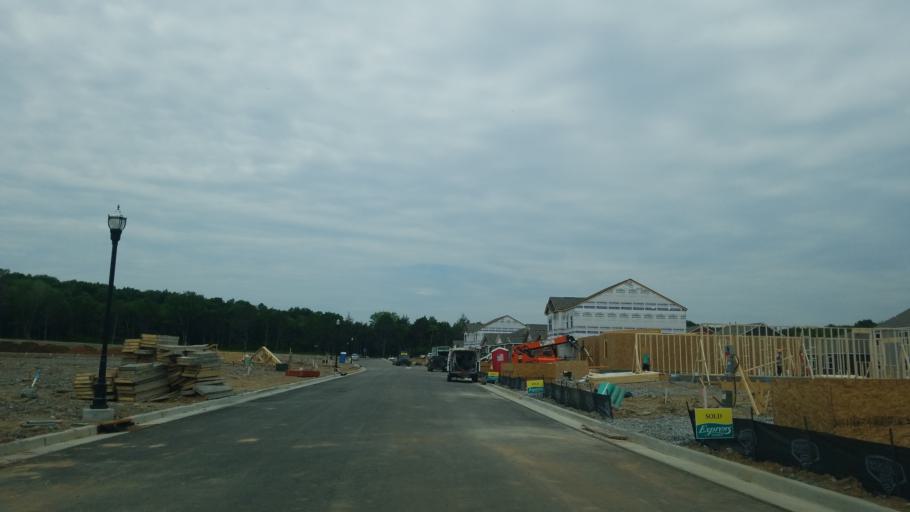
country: US
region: Tennessee
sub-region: Rutherford County
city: La Vergne
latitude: 36.0438
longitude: -86.5967
